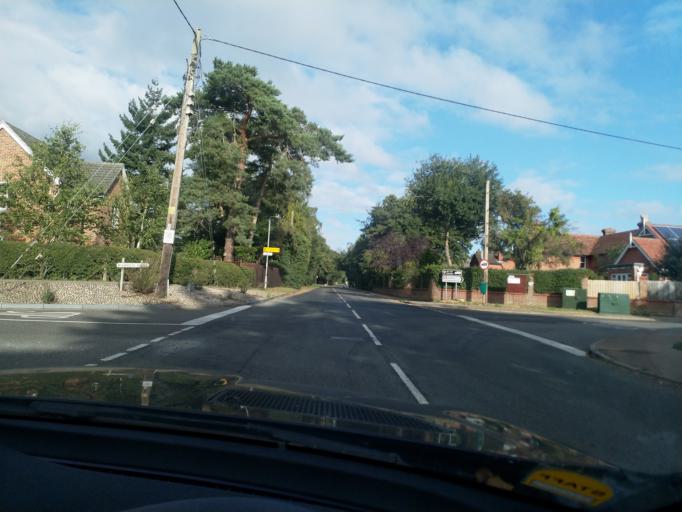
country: GB
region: England
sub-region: Suffolk
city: Elmswell
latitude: 52.2328
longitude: 0.9114
